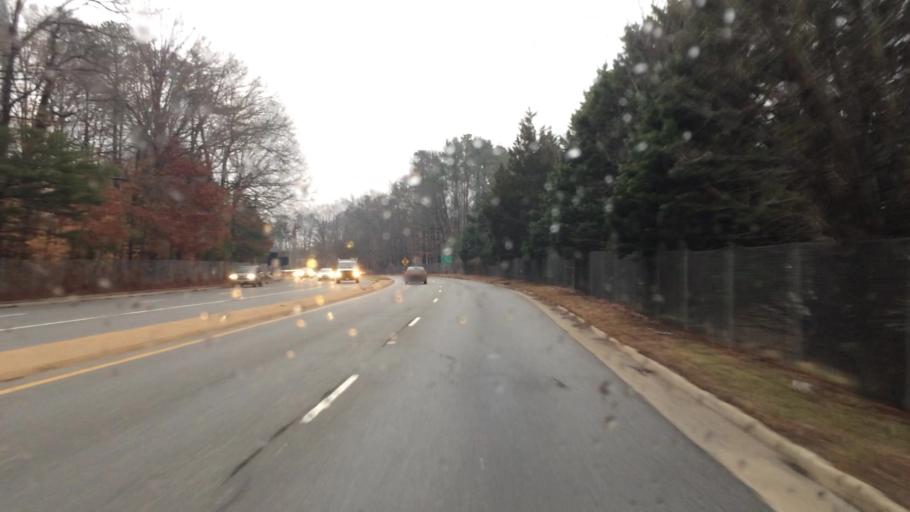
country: US
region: Virginia
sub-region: James City County
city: Williamsburg
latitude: 37.2528
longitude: -76.7305
